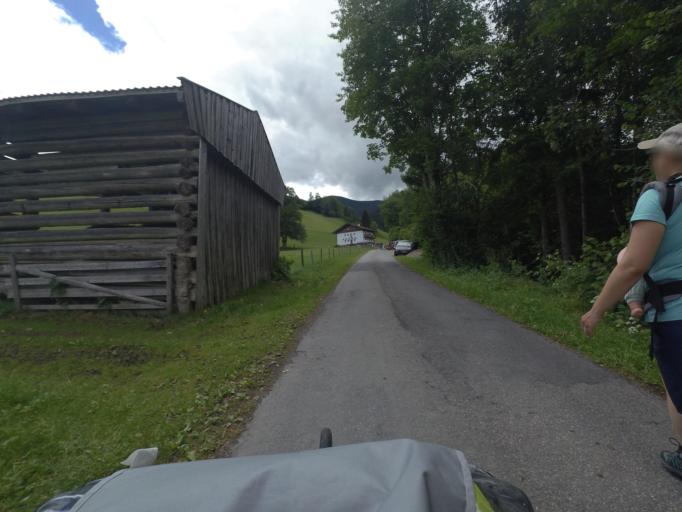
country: AT
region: Salzburg
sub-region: Politischer Bezirk Zell am See
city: Leogang
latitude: 47.4331
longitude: 12.7673
